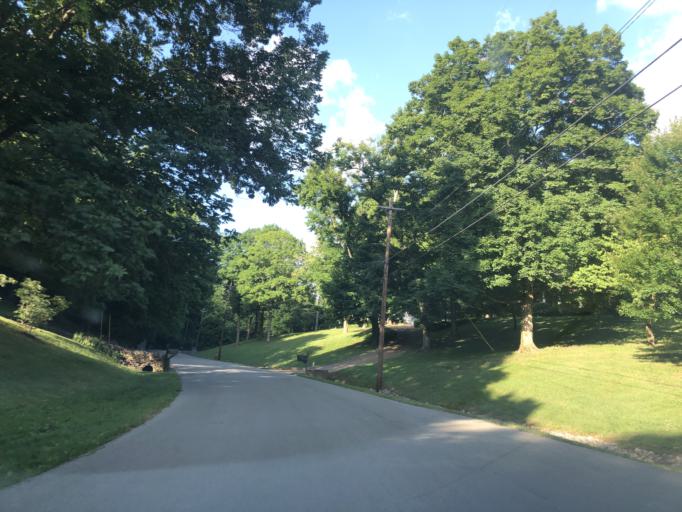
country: US
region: Tennessee
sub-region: Davidson County
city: Forest Hills
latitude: 36.0693
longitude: -86.8241
